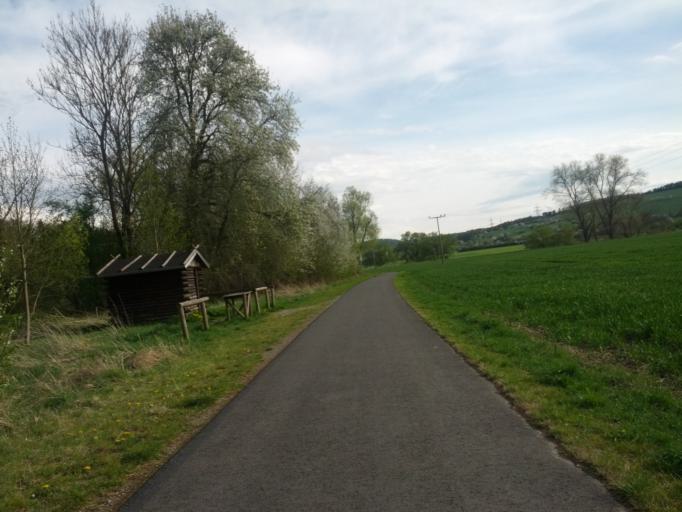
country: DE
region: Thuringia
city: Creuzburg
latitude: 51.0363
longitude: 10.2276
